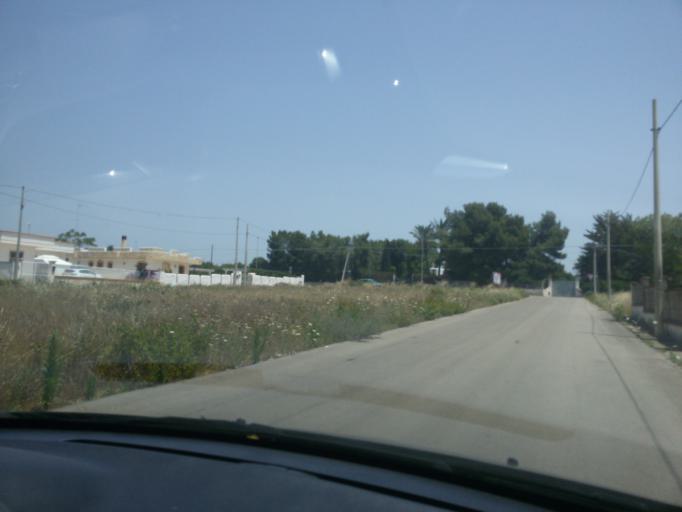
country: IT
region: Apulia
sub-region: Provincia di Lecce
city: Porto Cesareo
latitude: 40.2379
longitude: 17.9159
